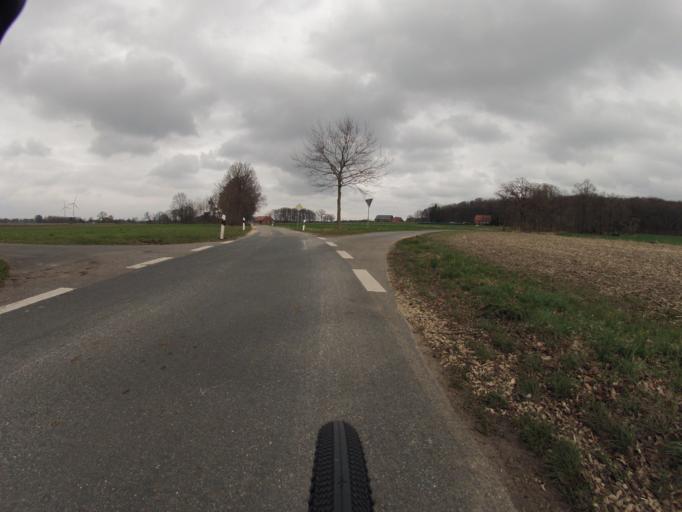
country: DE
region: North Rhine-Westphalia
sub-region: Regierungsbezirk Munster
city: Mettingen
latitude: 52.3264
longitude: 7.8225
